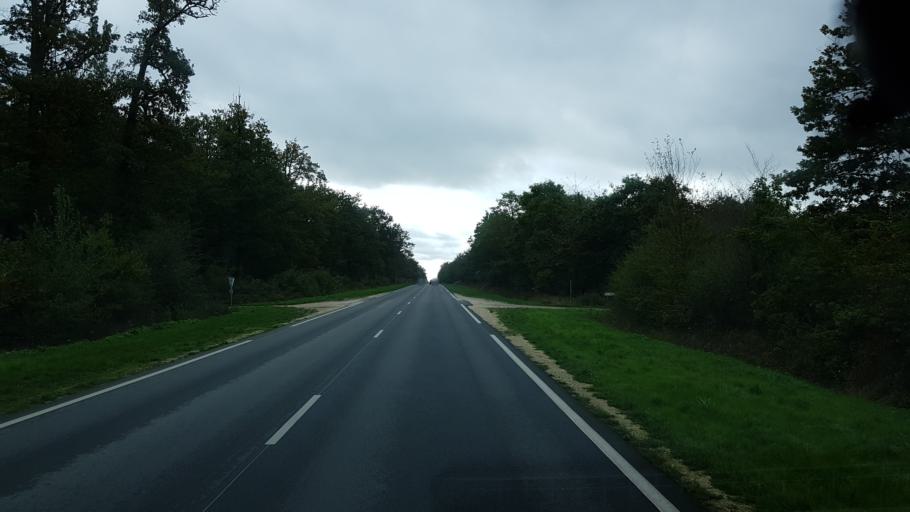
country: FR
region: Centre
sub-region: Departement du Loir-et-Cher
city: Theillay
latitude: 47.2657
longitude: 2.0598
